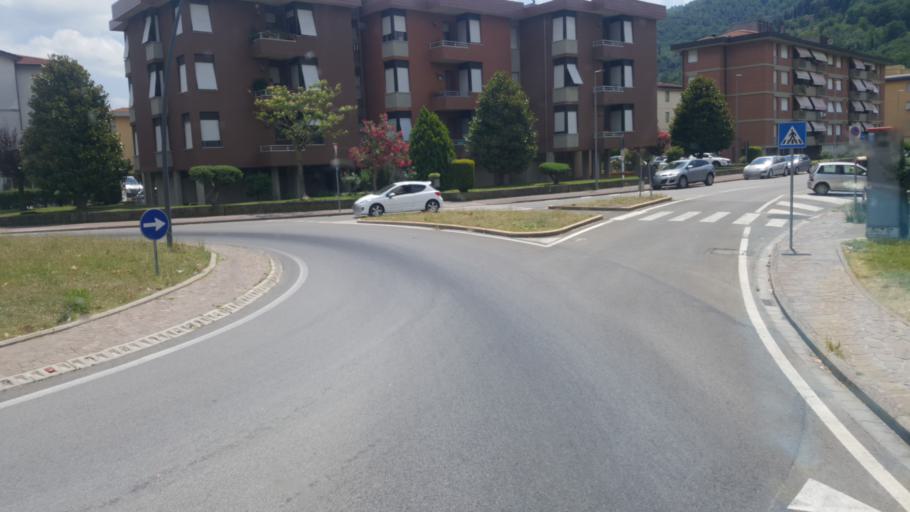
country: IT
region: Tuscany
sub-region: Province of Florence
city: Sieci
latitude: 43.7865
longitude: 11.3975
